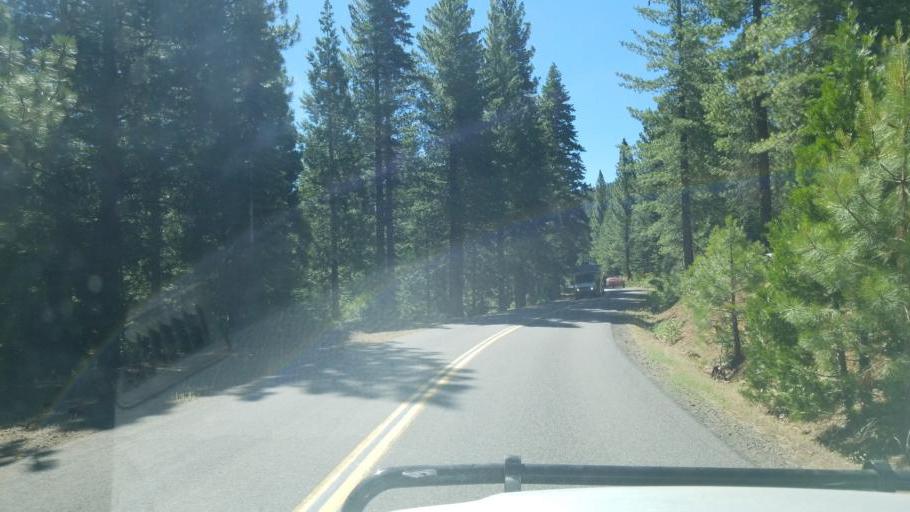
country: US
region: California
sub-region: Lassen County
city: Susanville
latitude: 40.5140
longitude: -120.7797
